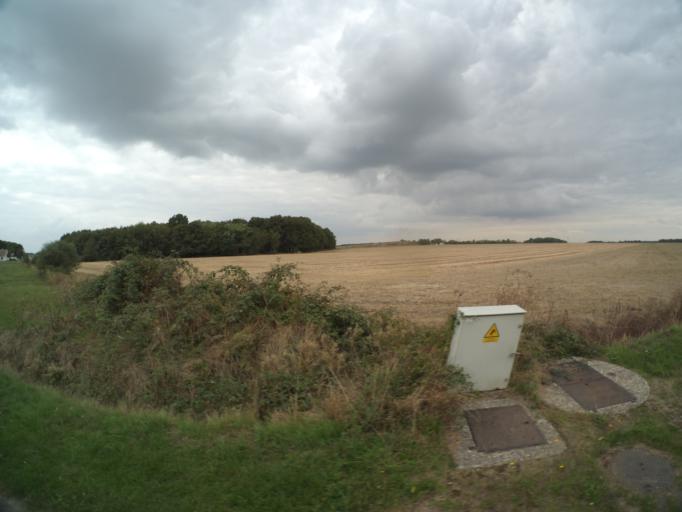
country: FR
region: Centre
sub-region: Departement d'Indre-et-Loire
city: Nazelles-Negron
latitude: 47.4904
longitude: 0.9460
